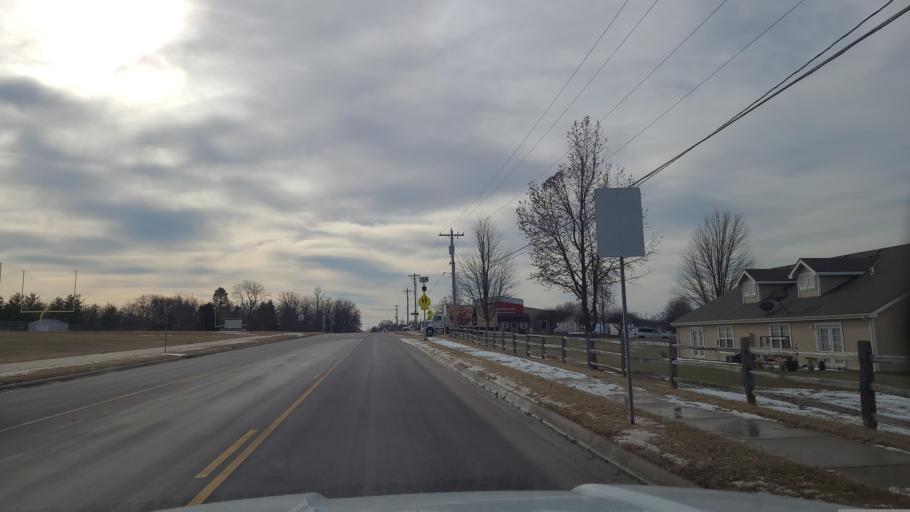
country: US
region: Kansas
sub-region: Douglas County
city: Baldwin City
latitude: 38.7871
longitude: -95.1865
